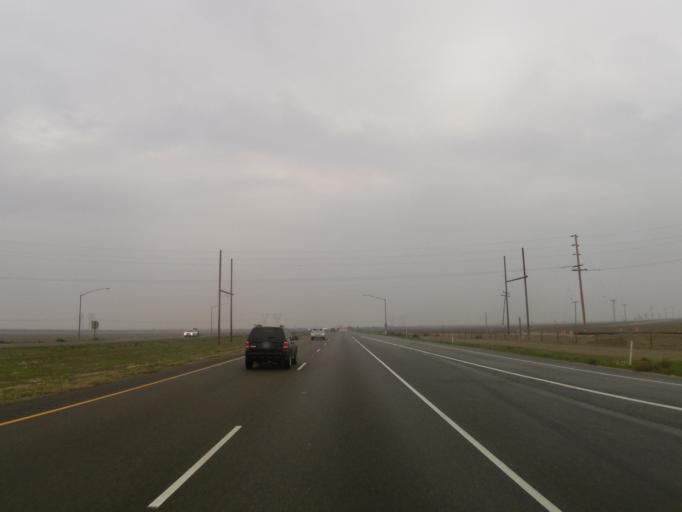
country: US
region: California
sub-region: Kern County
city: Greenfield
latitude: 35.0963
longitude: -119.0384
